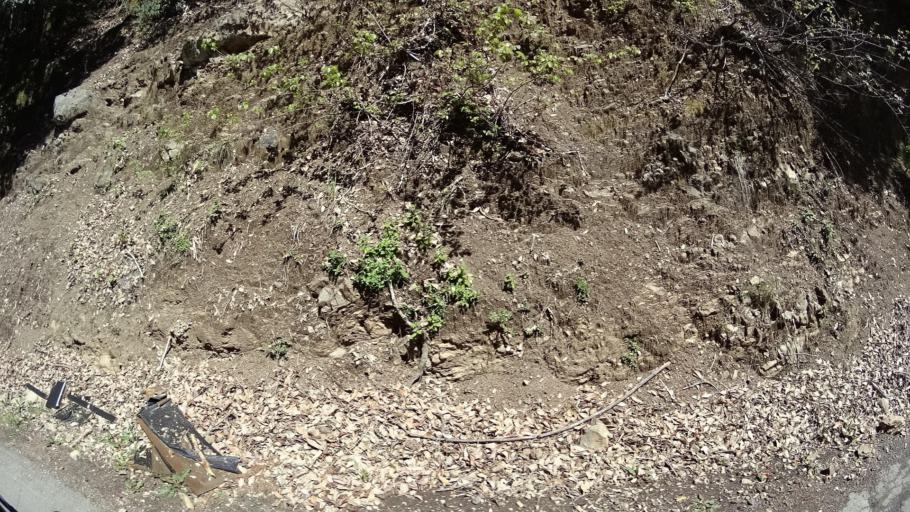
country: US
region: California
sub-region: Humboldt County
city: Rio Dell
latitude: 40.2686
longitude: -124.0819
